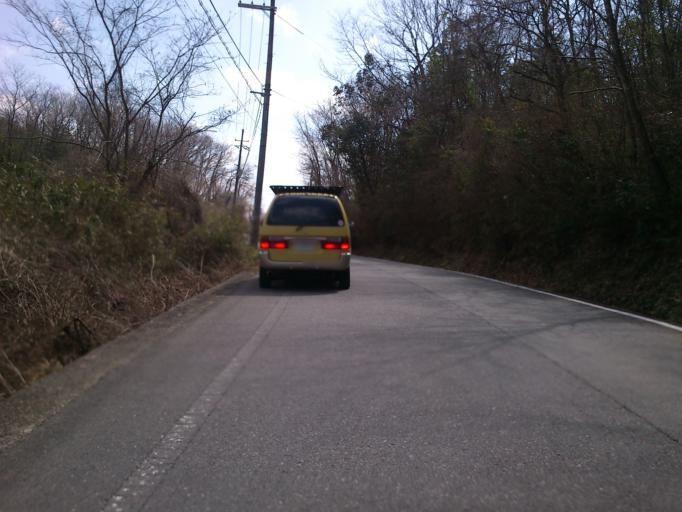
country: JP
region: Mie
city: Ueno-ebisumachi
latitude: 34.7539
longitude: 136.0249
